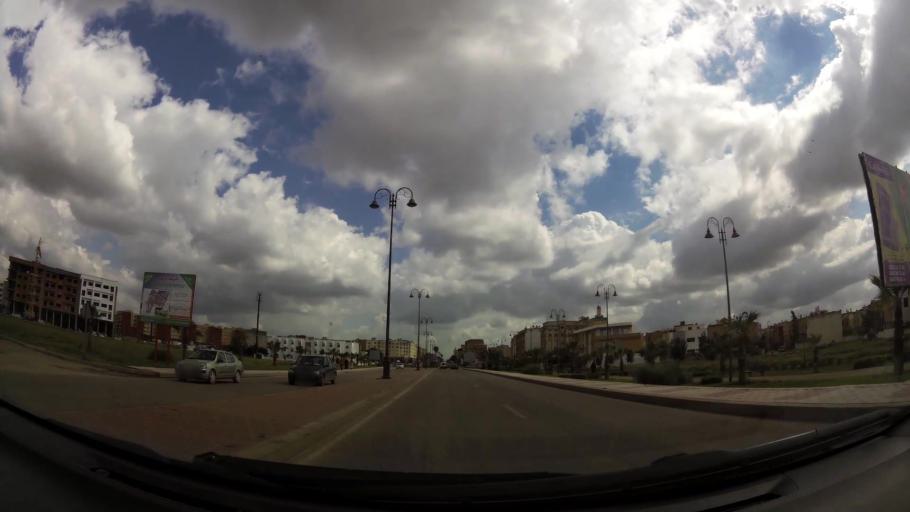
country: MA
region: Chaouia-Ouardigha
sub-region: Settat Province
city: Berrechid
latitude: 33.2785
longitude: -7.5892
